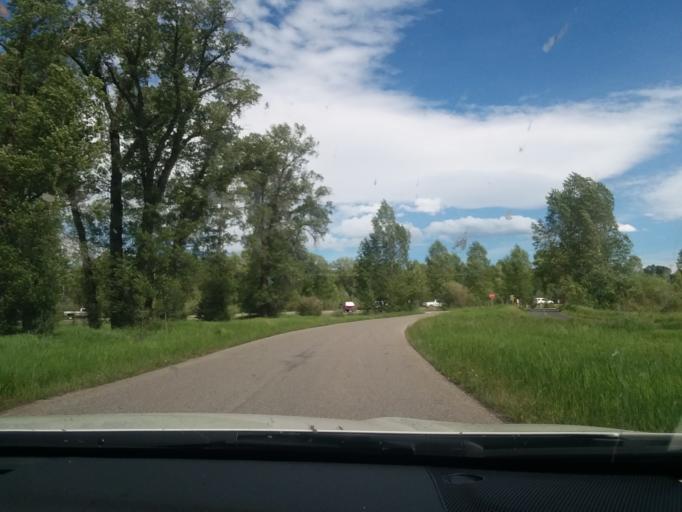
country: US
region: Wyoming
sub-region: Teton County
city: Moose Wilson Road
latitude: 43.5030
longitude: -110.8477
